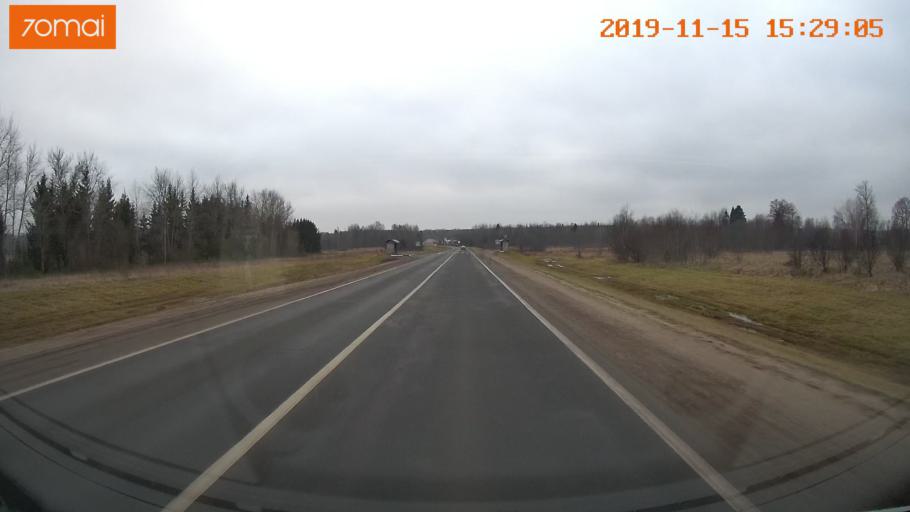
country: RU
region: Jaroslavl
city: Danilov
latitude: 58.1247
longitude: 40.1250
